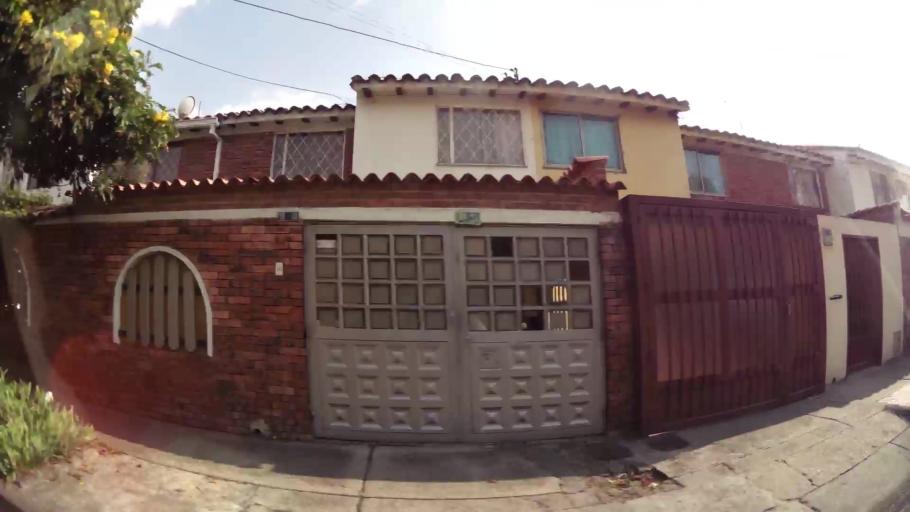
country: CO
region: Bogota D.C.
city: Barrio San Luis
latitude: 4.7307
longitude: -74.0566
